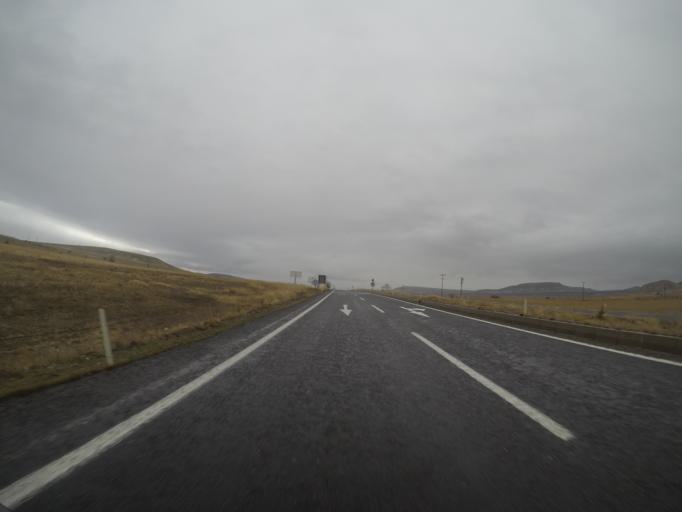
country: TR
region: Nevsehir
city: Avanos
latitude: 38.7145
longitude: 34.9334
